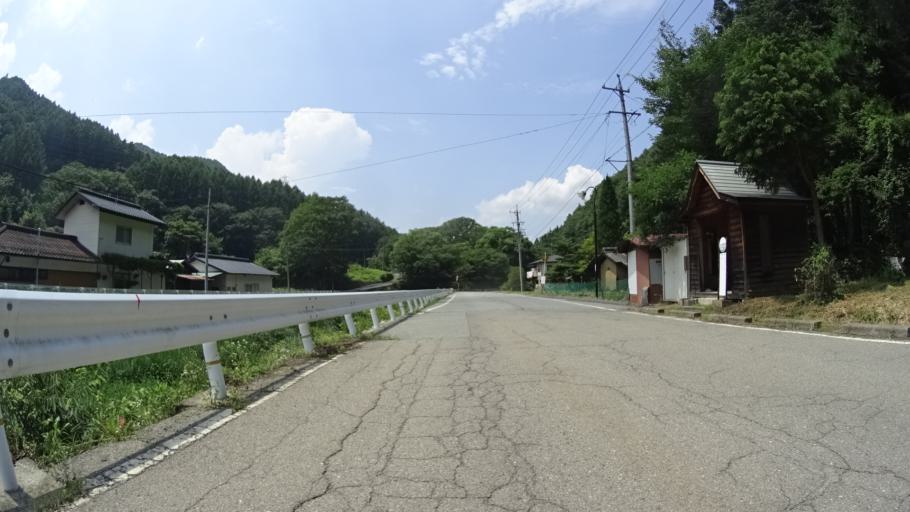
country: JP
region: Nagano
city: Saku
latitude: 36.1293
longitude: 138.5788
